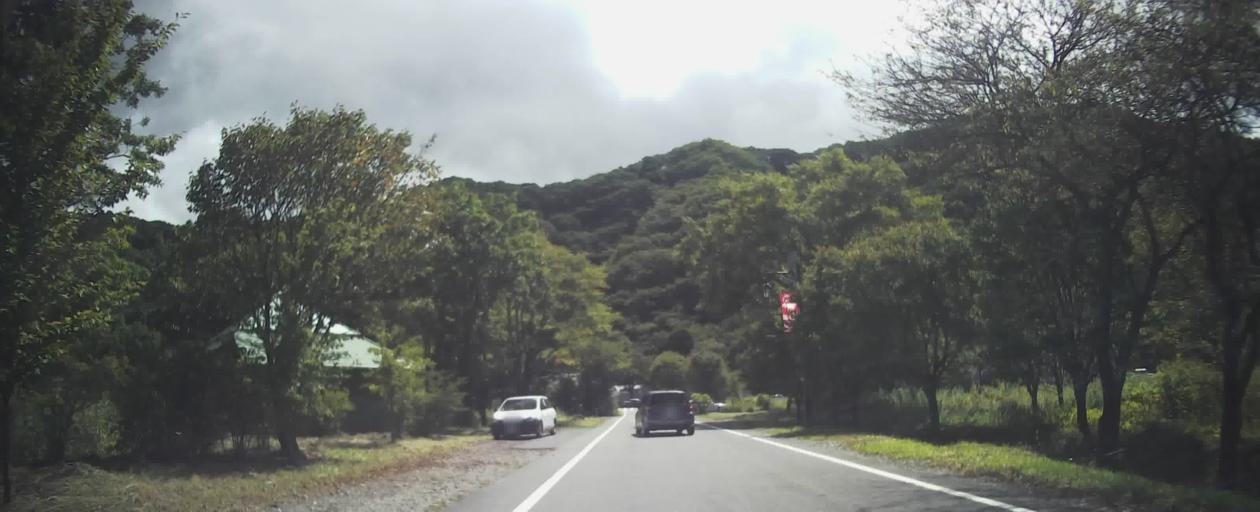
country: JP
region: Gunma
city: Nakanojomachi
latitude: 36.4690
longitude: 138.8736
